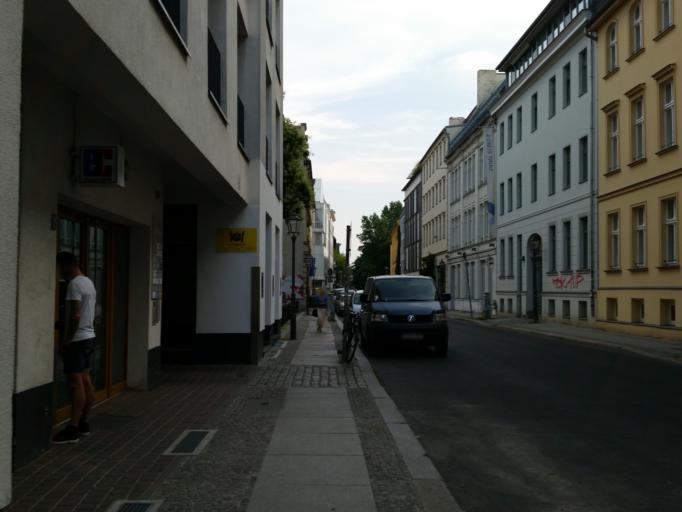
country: DE
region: Berlin
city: Berlin
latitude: 52.5284
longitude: 13.4051
